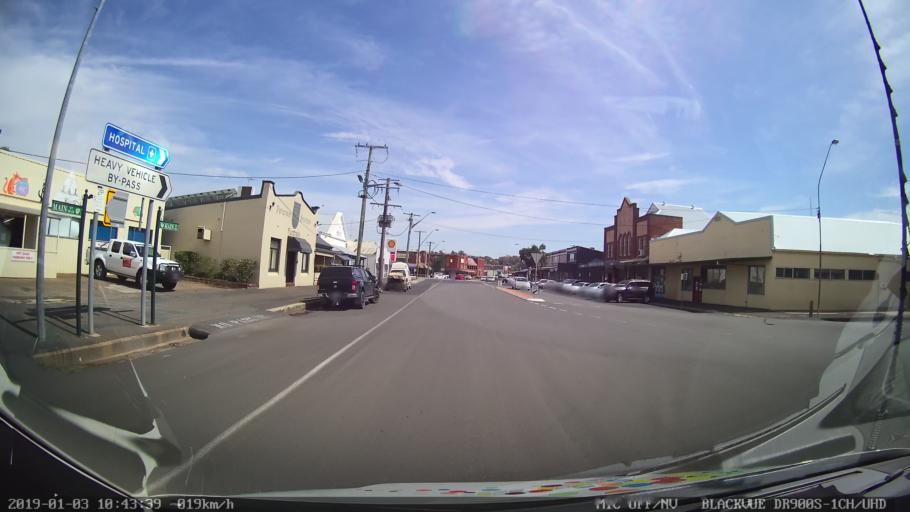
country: AU
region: New South Wales
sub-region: Young
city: Young
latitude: -34.3143
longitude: 148.2957
